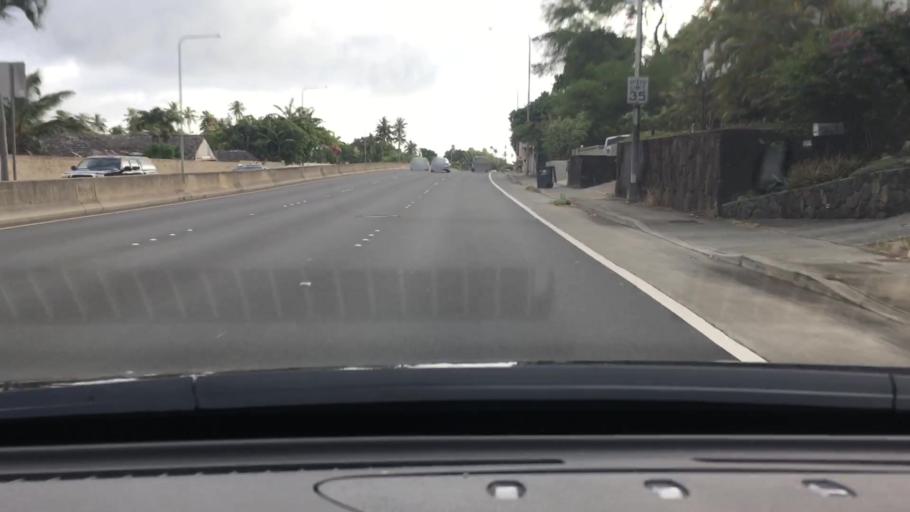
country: US
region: Hawaii
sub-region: Honolulu County
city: Waimanalo Beach
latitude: 21.2850
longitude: -157.7268
